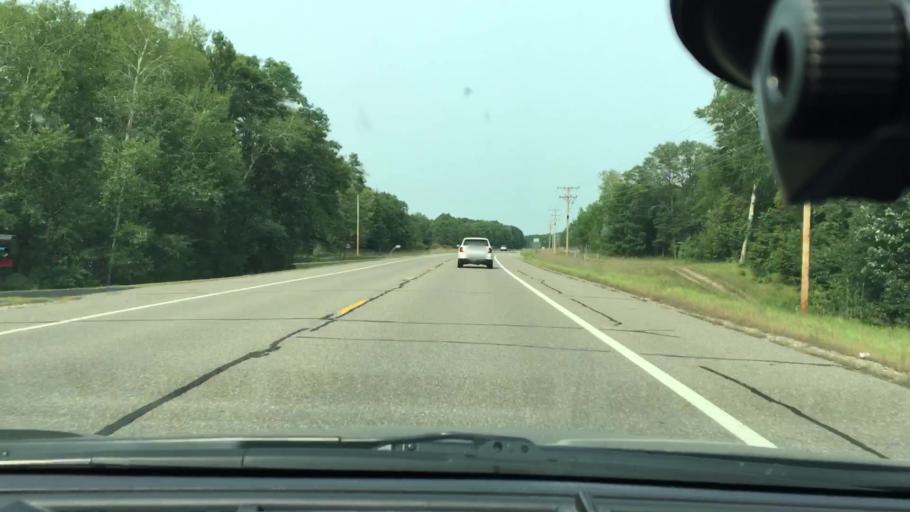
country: US
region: Minnesota
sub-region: Crow Wing County
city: Cross Lake
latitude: 46.5941
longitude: -94.1316
